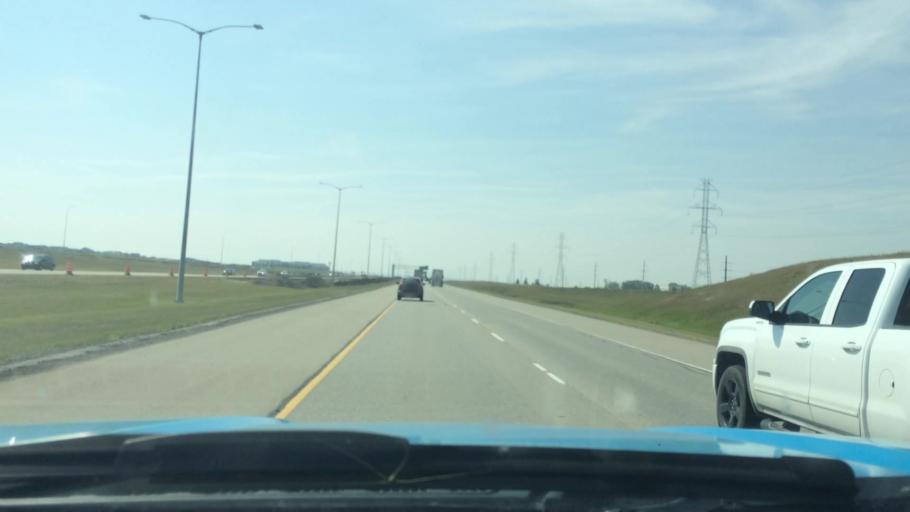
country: CA
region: Alberta
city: Airdrie
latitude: 51.1759
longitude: -113.9434
